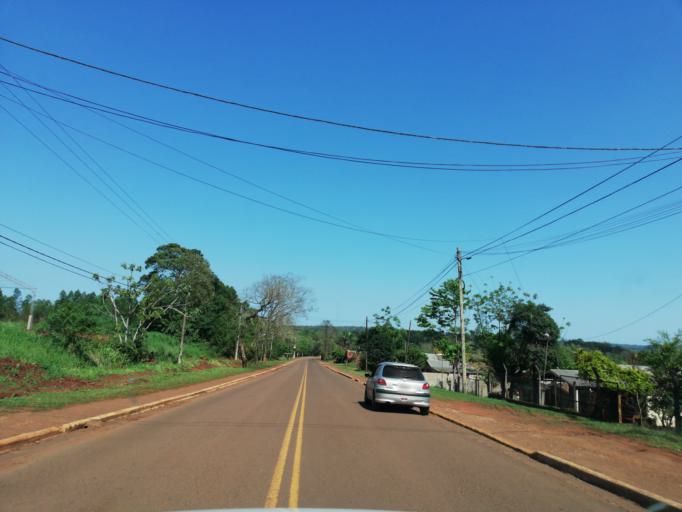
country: AR
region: Misiones
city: Puerto Eldorado
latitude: -26.4110
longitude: -54.6818
